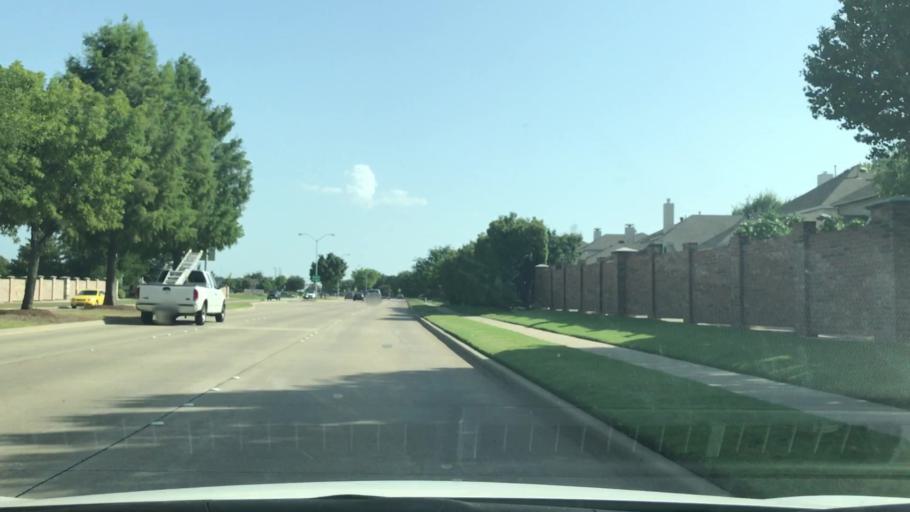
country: US
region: Texas
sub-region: Collin County
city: Allen
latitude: 33.0904
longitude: -96.7493
